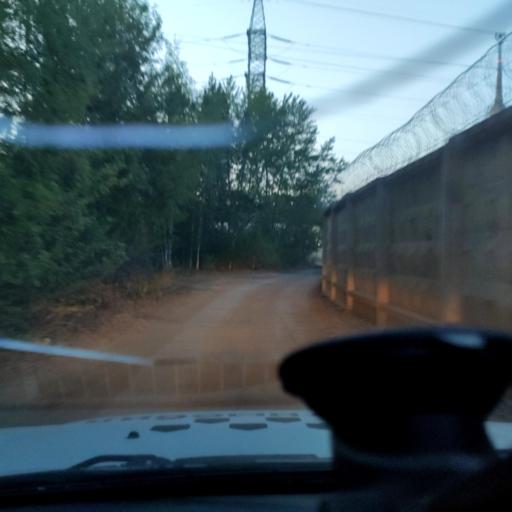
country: RU
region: Perm
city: Perm
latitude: 58.1135
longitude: 56.3427
